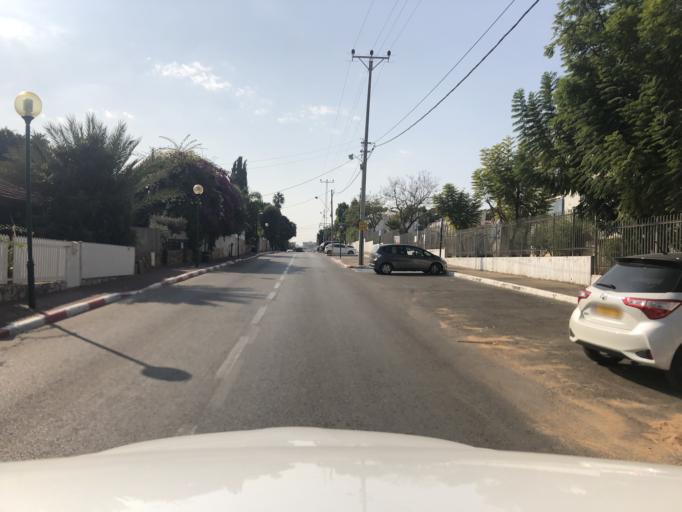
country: IL
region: Central District
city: Kfar Saba
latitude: 32.1839
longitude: 34.9077
